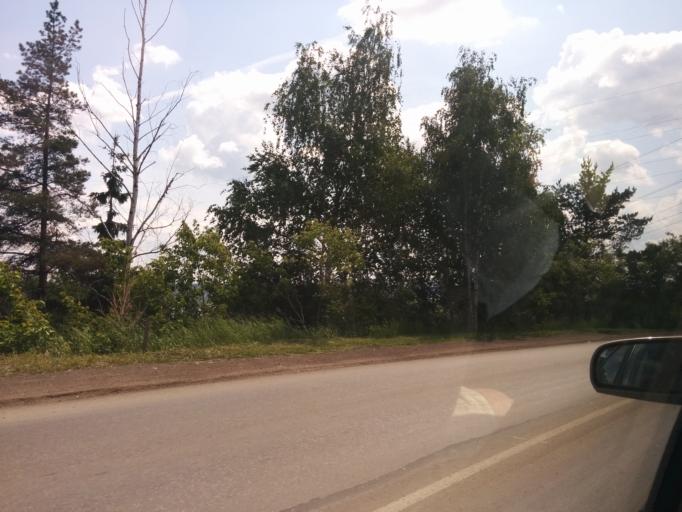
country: RU
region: Perm
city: Perm
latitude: 58.1143
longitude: 56.3228
